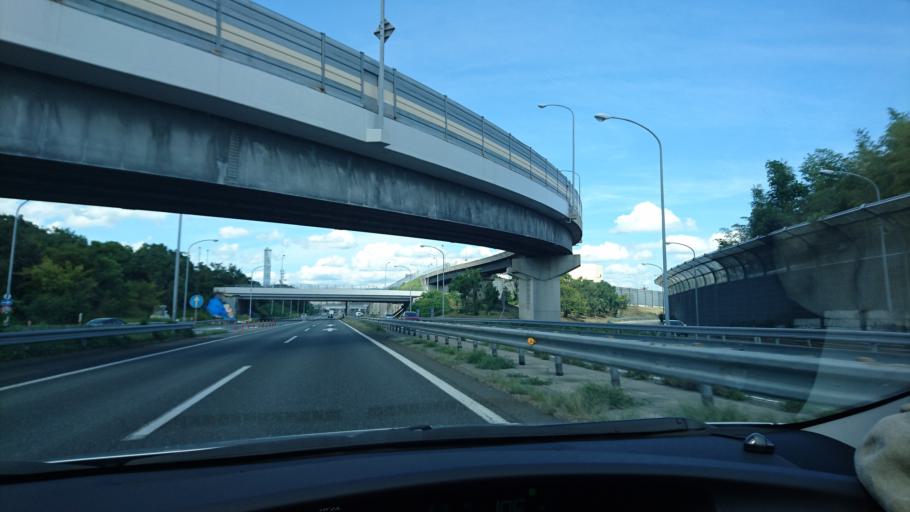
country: JP
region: Osaka
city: Ibaraki
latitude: 34.8027
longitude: 135.5412
